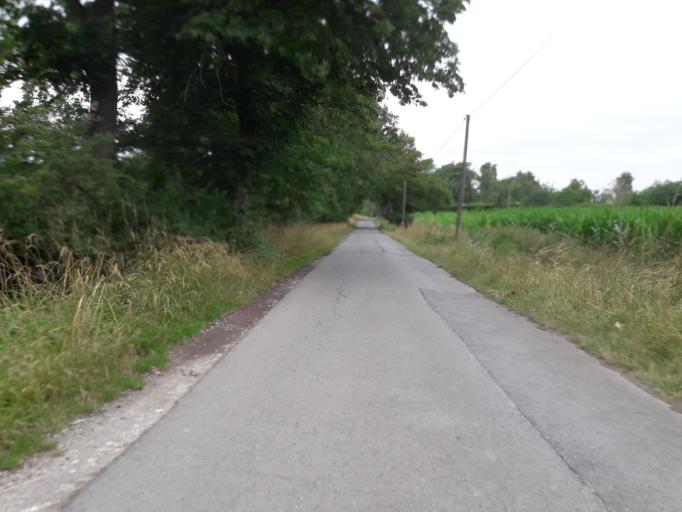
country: DE
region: North Rhine-Westphalia
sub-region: Regierungsbezirk Detmold
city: Salzkotten
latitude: 51.7206
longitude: 8.6436
